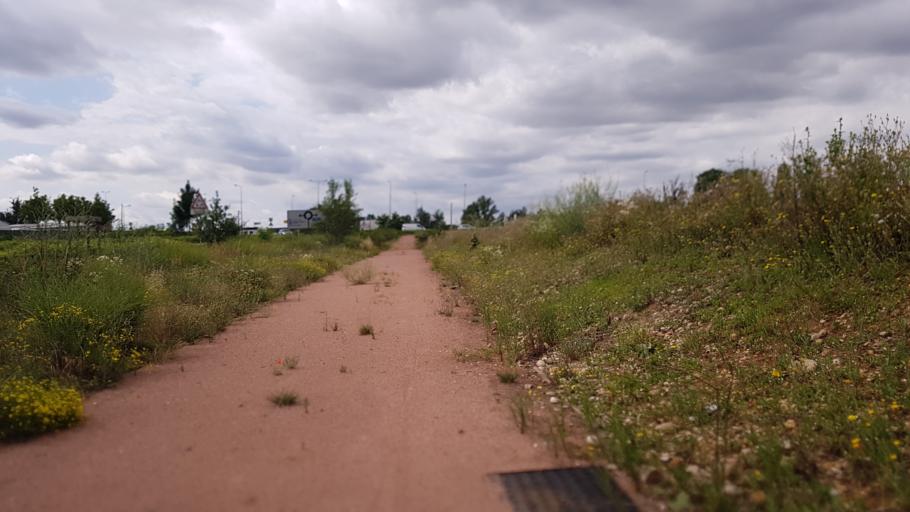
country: FR
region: Rhone-Alpes
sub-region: Departement du Rhone
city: Saint-Priest
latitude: 45.7197
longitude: 4.9547
